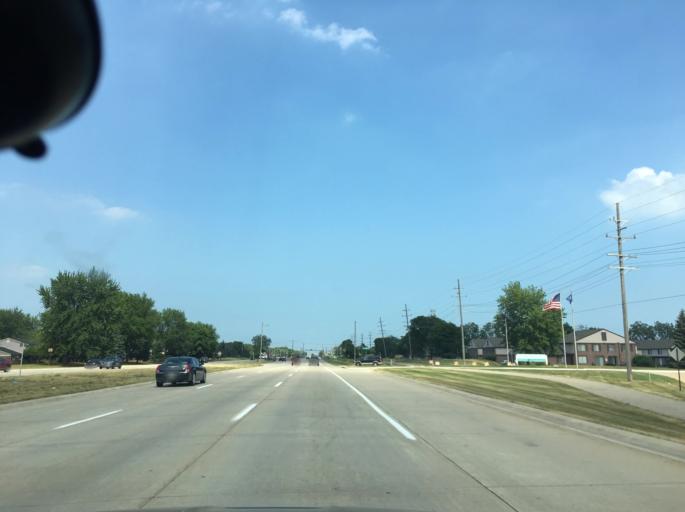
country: US
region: Michigan
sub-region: Macomb County
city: Clinton
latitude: 42.5689
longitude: -82.9209
